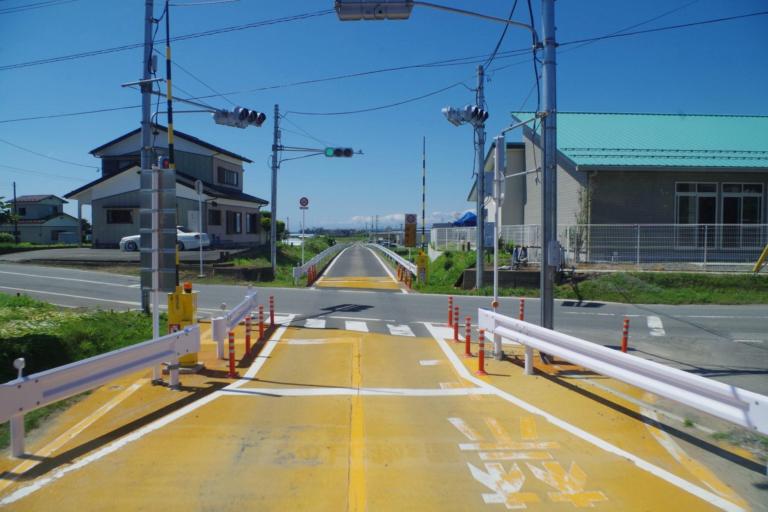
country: JP
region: Iwate
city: Ofunato
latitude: 38.8349
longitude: 141.5800
